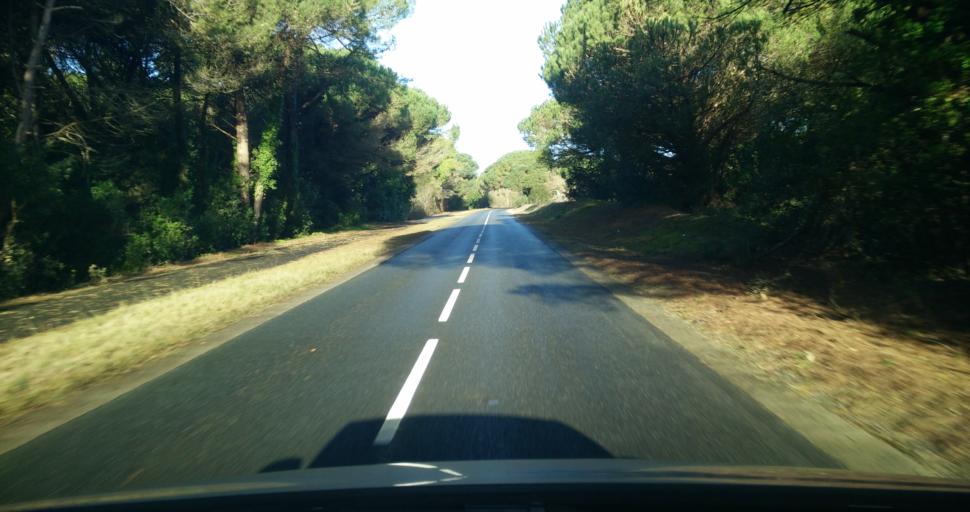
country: FR
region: Poitou-Charentes
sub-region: Departement de la Charente-Maritime
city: La Flotte
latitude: 46.1711
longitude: -1.3271
